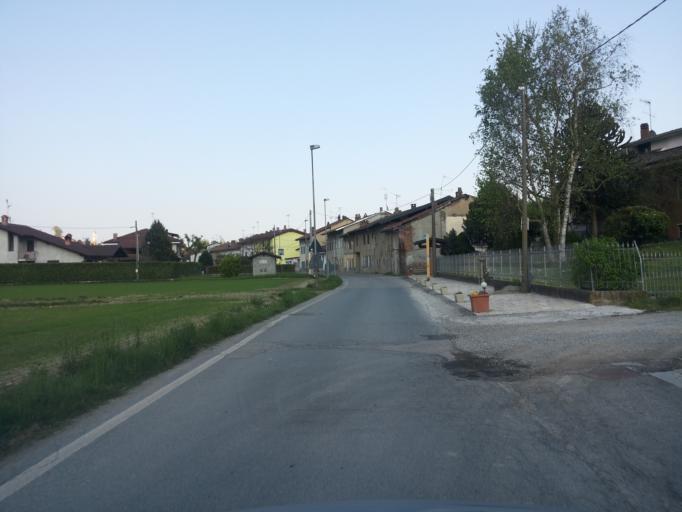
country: IT
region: Piedmont
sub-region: Provincia di Torino
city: Azeglio
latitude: 45.4211
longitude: 7.9799
